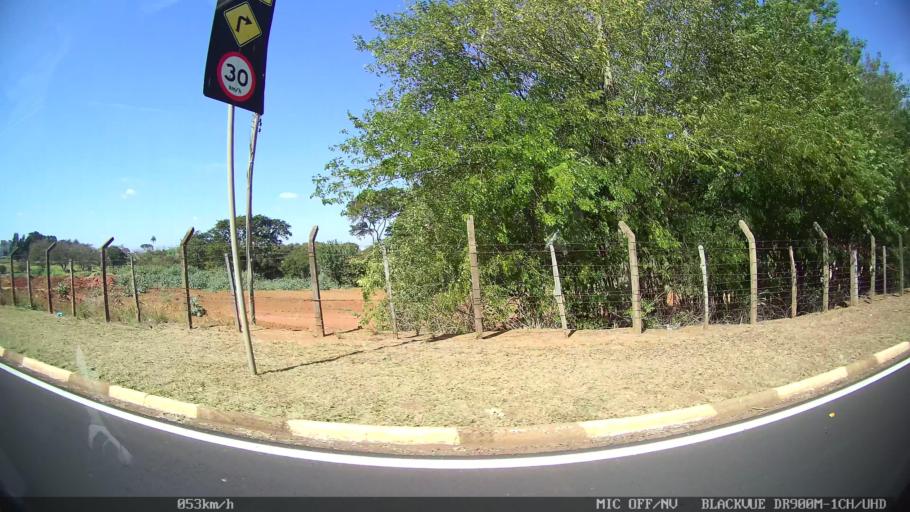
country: BR
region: Sao Paulo
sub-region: Franca
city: Franca
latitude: -20.5447
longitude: -47.4232
